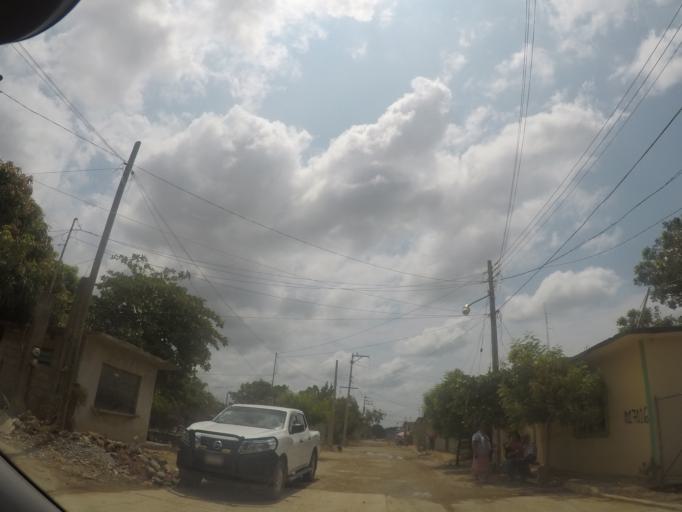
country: MX
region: Oaxaca
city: El Espinal
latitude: 16.5524
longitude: -94.9432
